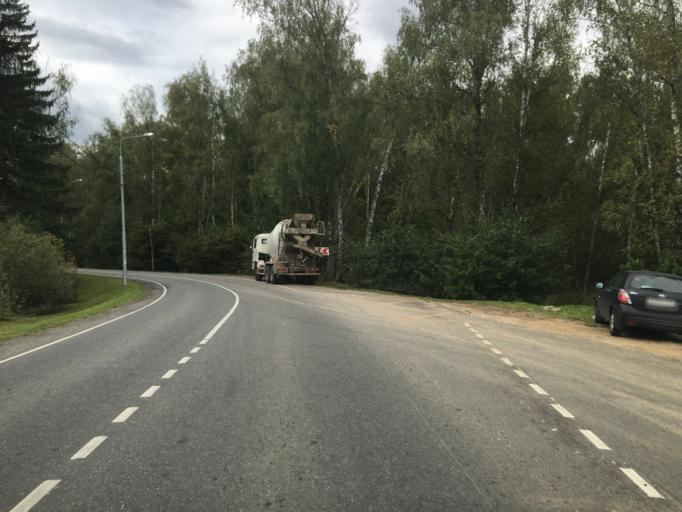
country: RU
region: Moskovskaya
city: Vatutinki
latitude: 55.4991
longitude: 37.3852
